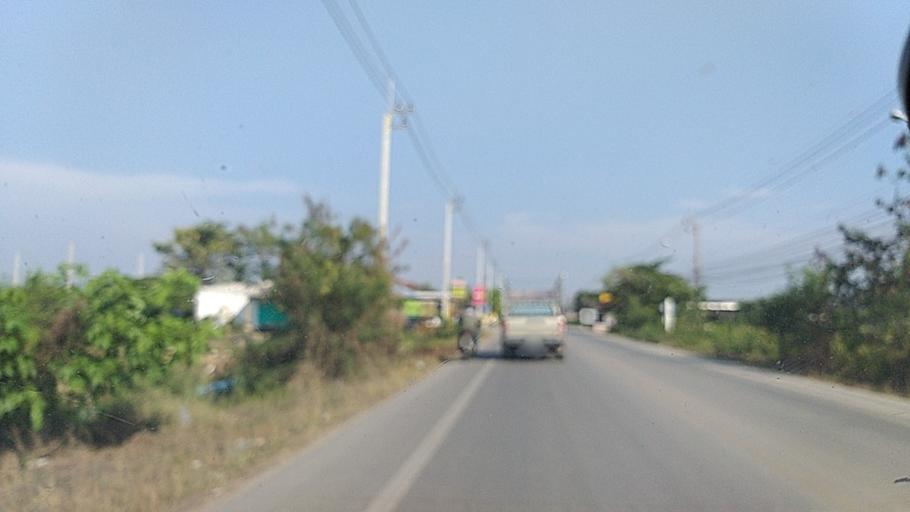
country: TH
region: Nonthaburi
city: Sai Noi
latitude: 13.9429
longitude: 100.3588
